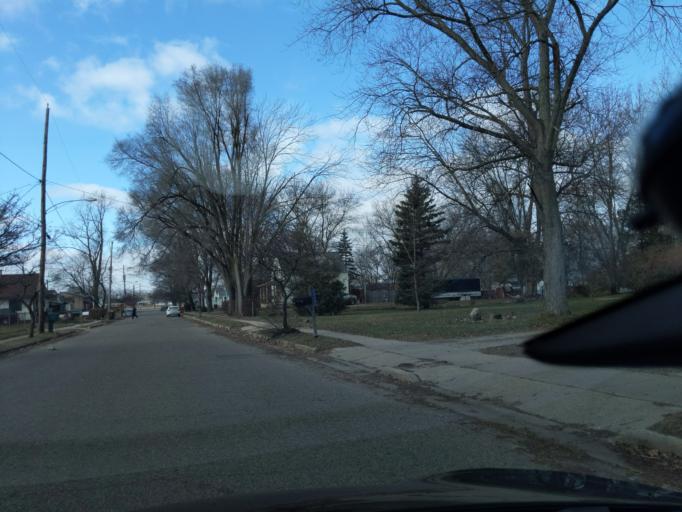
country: US
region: Michigan
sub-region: Ingham County
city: Lansing
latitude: 42.6718
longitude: -84.5846
